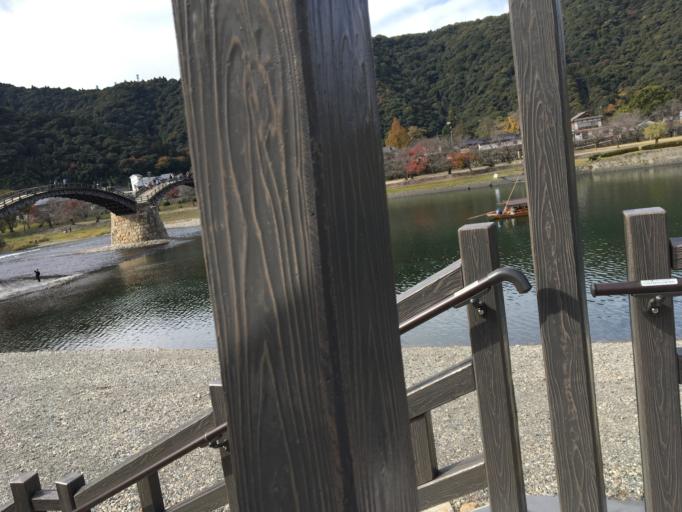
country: JP
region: Yamaguchi
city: Iwakuni
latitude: 34.1677
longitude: 132.1795
